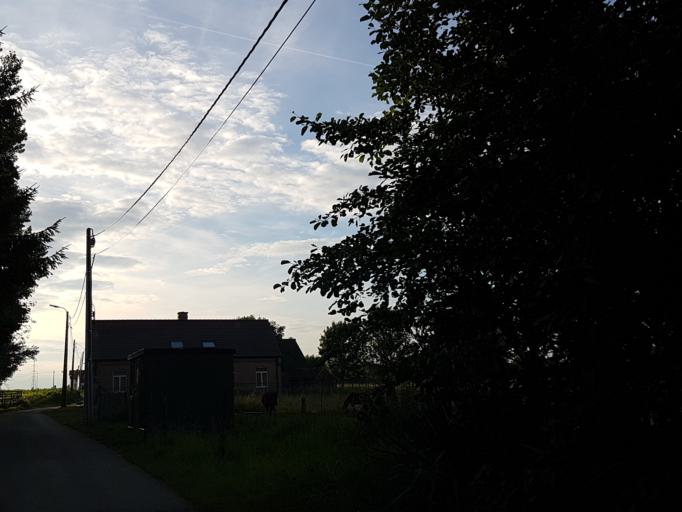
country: BE
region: Flanders
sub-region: Provincie Vlaams-Brabant
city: Merchtem
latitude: 50.9792
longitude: 4.2557
